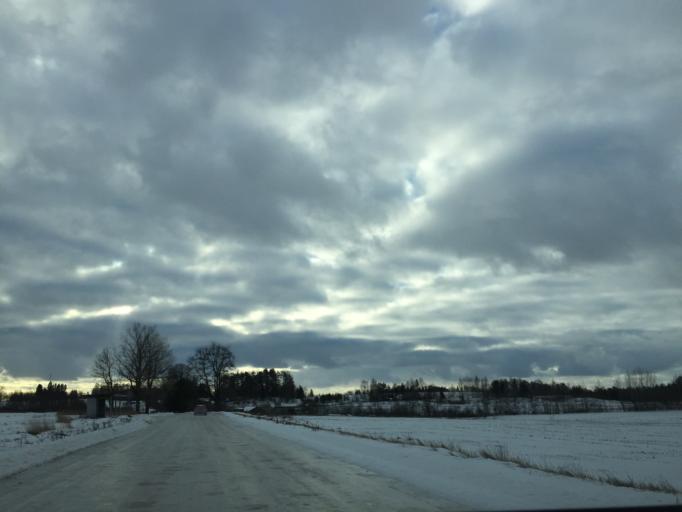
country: LV
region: Lielvarde
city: Lielvarde
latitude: 56.5848
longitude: 24.7343
